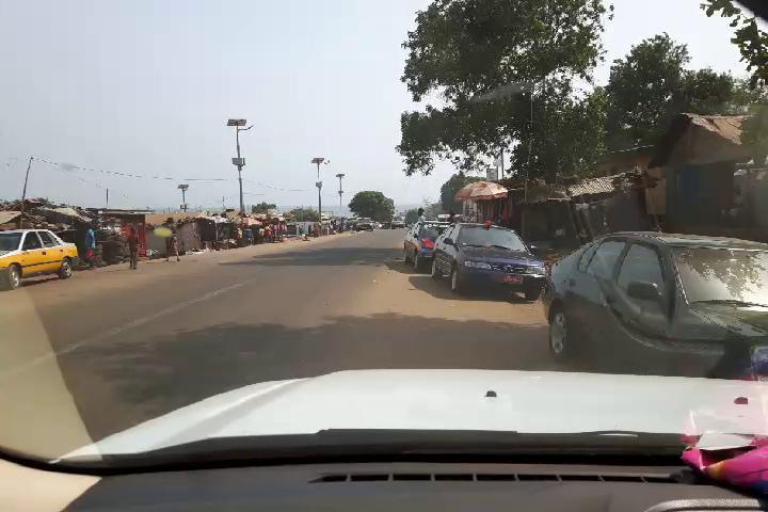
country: SL
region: Western Area
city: Waterloo
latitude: 8.2148
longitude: -13.1000
